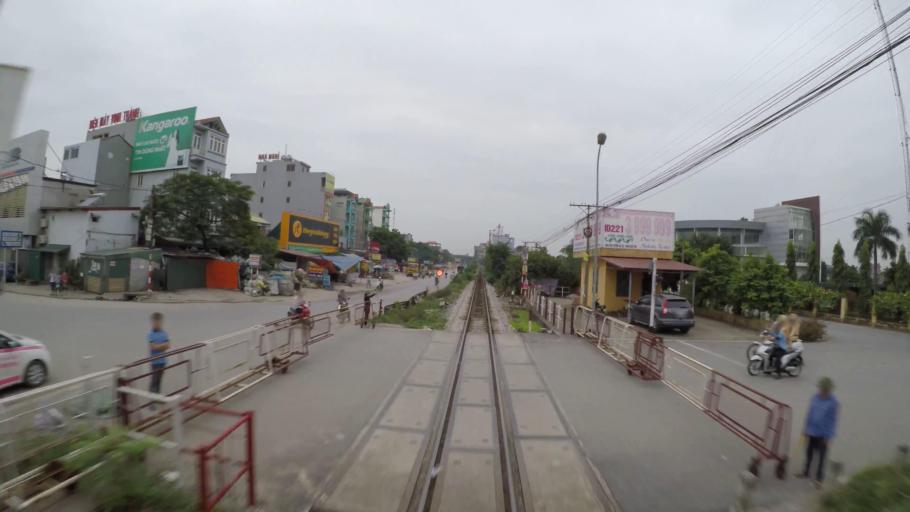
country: VN
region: Hung Yen
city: Nhu Quynh
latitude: 20.9765
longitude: 106.0076
